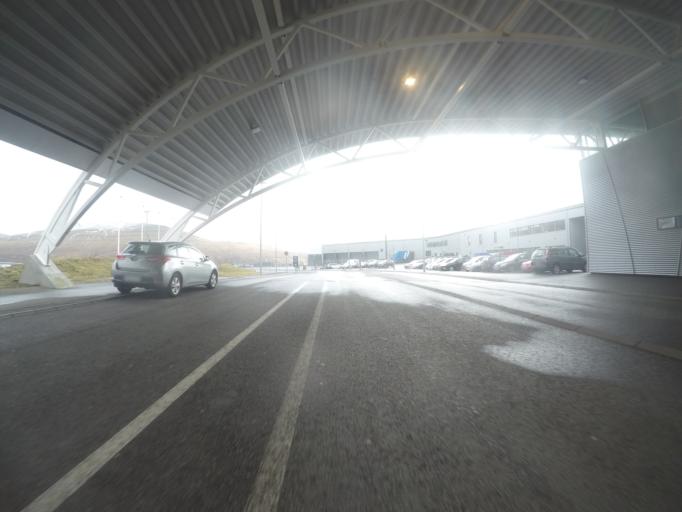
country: FO
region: Vagar
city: Sorvagur
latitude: 62.0676
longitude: -7.2781
